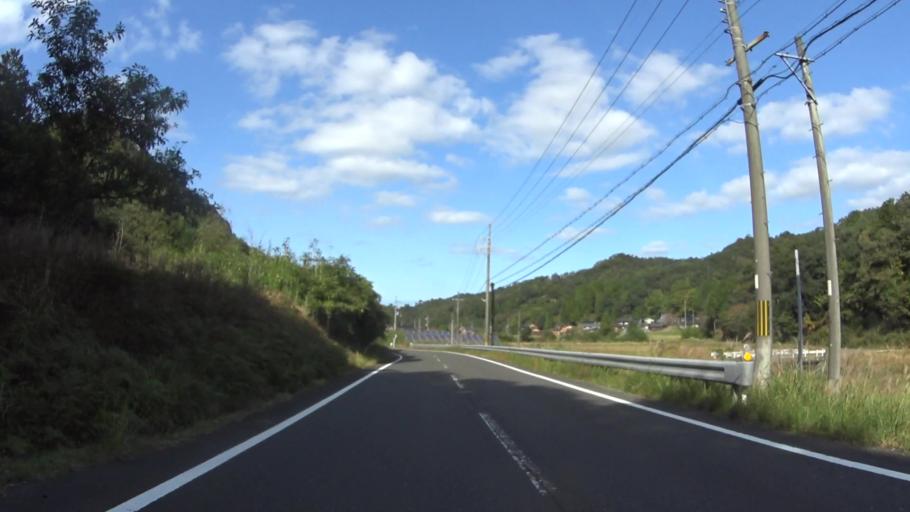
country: JP
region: Hyogo
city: Toyooka
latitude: 35.5592
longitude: 134.9796
